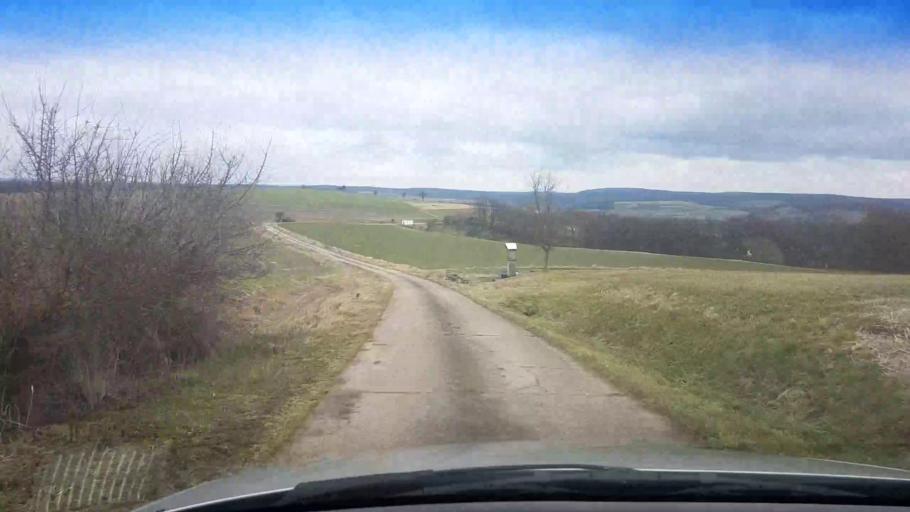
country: DE
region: Bavaria
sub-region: Regierungsbezirk Unterfranken
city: Stettfeld
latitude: 49.9398
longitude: 10.7141
